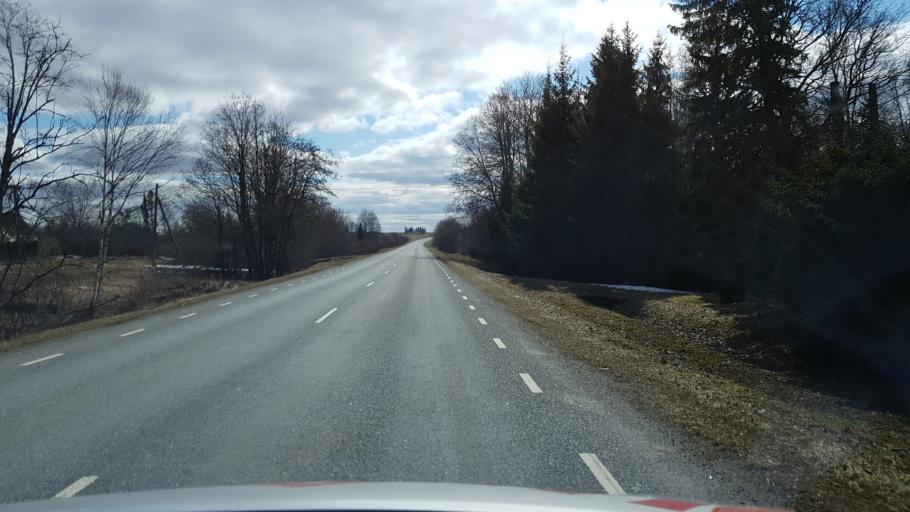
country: EE
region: Laeaene-Virumaa
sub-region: Kadrina vald
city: Kadrina
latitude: 59.3690
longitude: 26.1039
